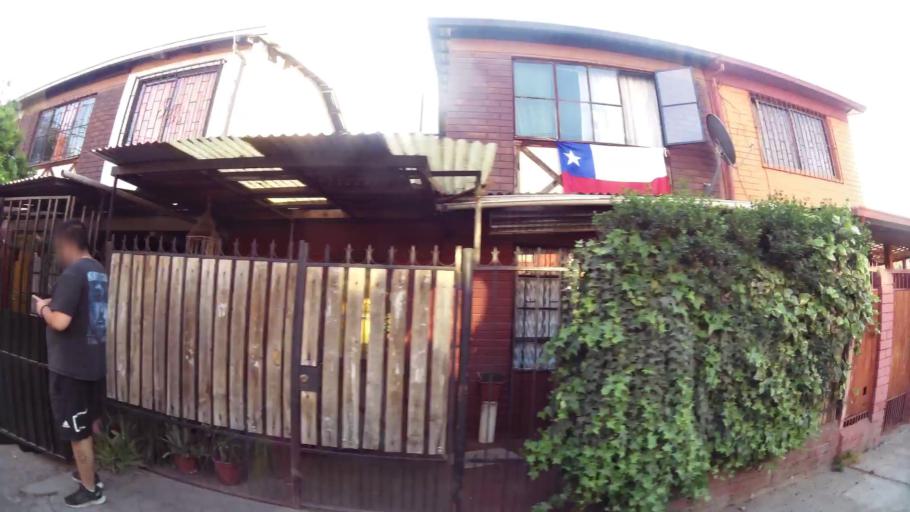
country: CL
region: Santiago Metropolitan
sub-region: Provincia de Santiago
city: La Pintana
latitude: -33.5479
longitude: -70.6192
